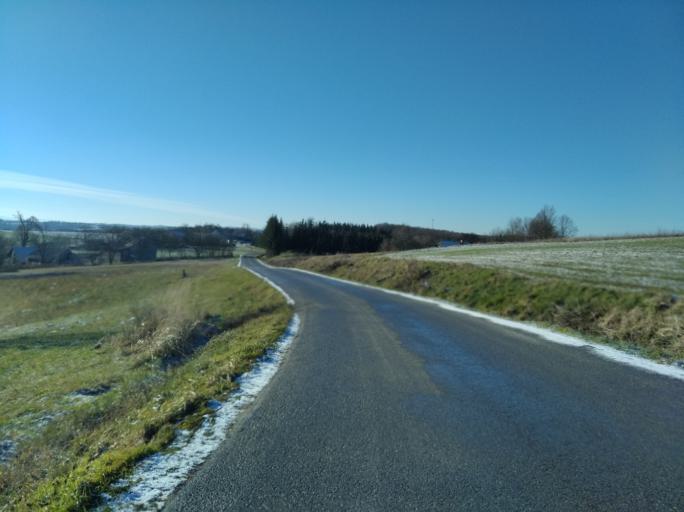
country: PL
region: Subcarpathian Voivodeship
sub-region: Powiat ropczycko-sedziszowski
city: Iwierzyce
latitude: 49.9706
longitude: 21.7533
